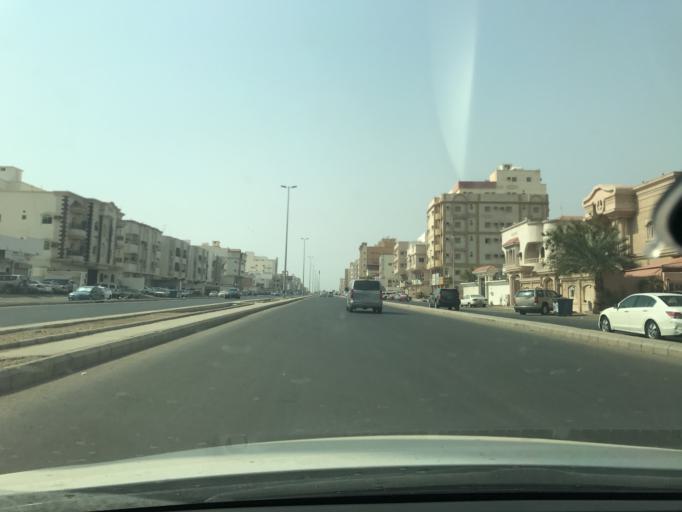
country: SA
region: Makkah
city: Jeddah
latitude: 21.6215
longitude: 39.1698
